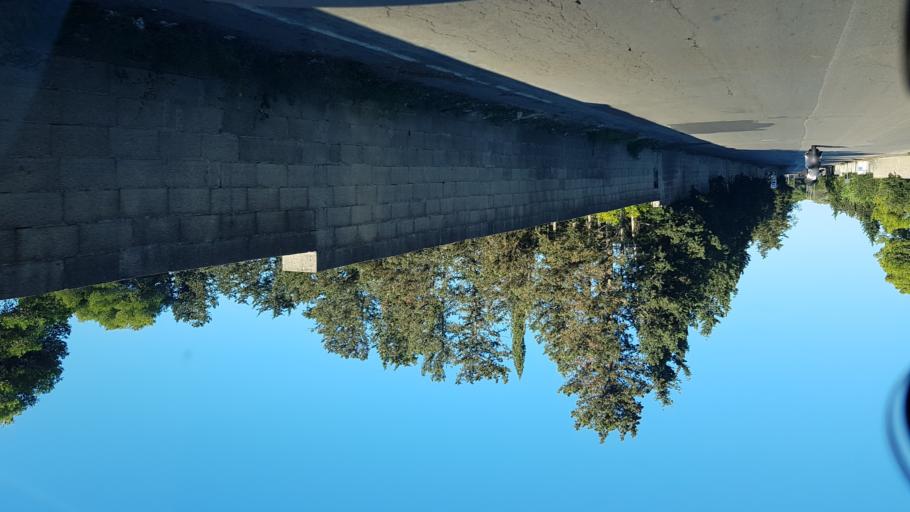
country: IT
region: Apulia
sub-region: Provincia di Lecce
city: San Pietro in Lama
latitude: 40.3394
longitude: 18.1312
